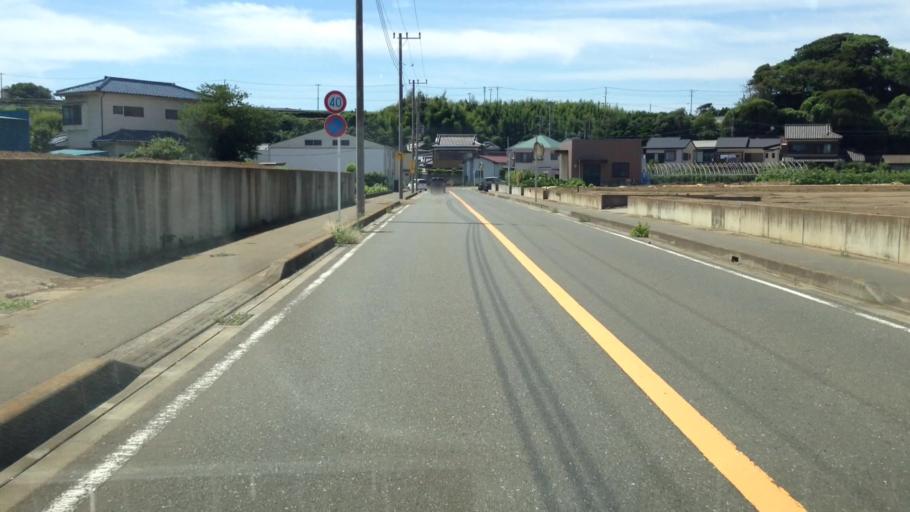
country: JP
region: Kanagawa
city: Miura
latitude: 35.1995
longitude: 139.6205
